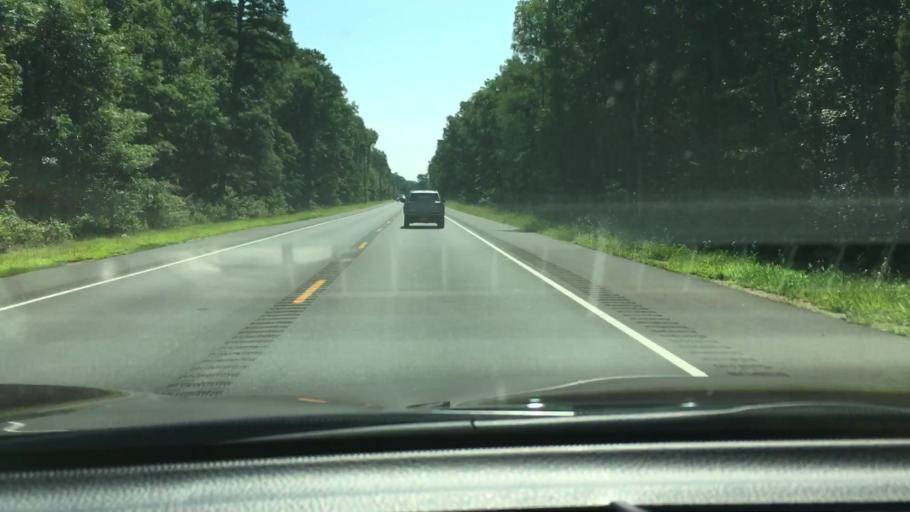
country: US
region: New Jersey
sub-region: Cape May County
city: Woodbine
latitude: 39.3145
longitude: -74.8304
